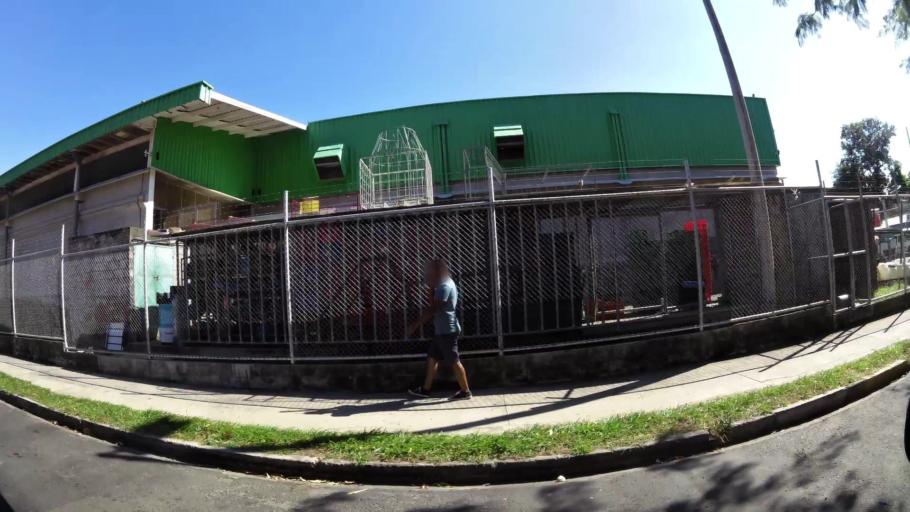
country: CR
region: Guanacaste
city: Liberia
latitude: 10.6315
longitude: -85.4432
